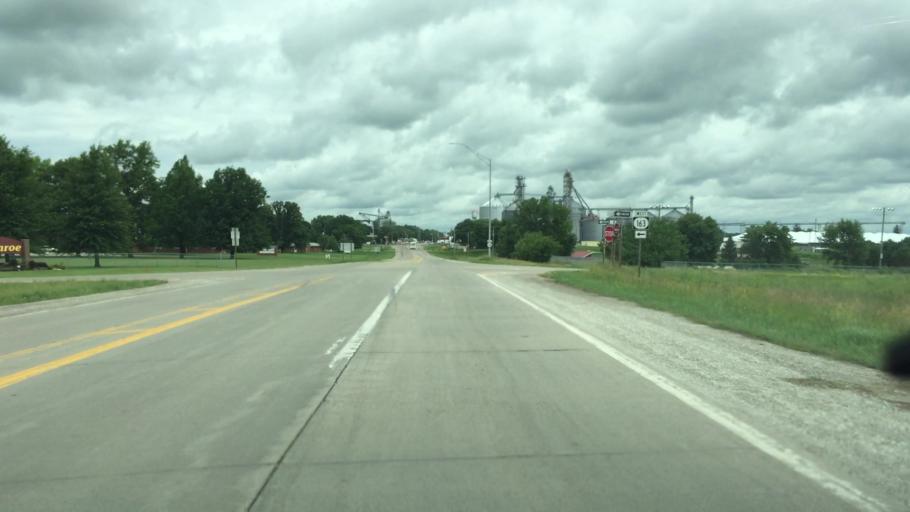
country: US
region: Iowa
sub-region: Jasper County
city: Monroe
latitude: 41.5120
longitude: -93.1012
